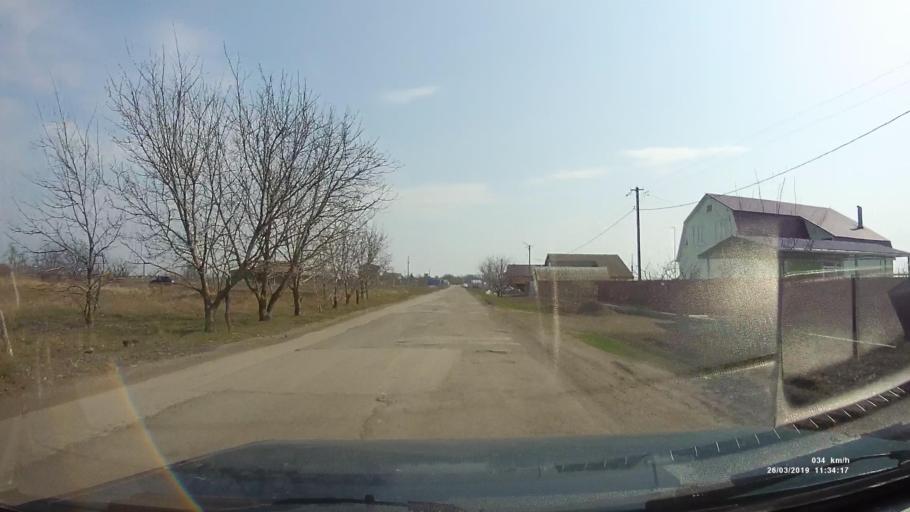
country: RU
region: Rostov
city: Novobessergenovka
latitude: 47.1471
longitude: 38.6290
